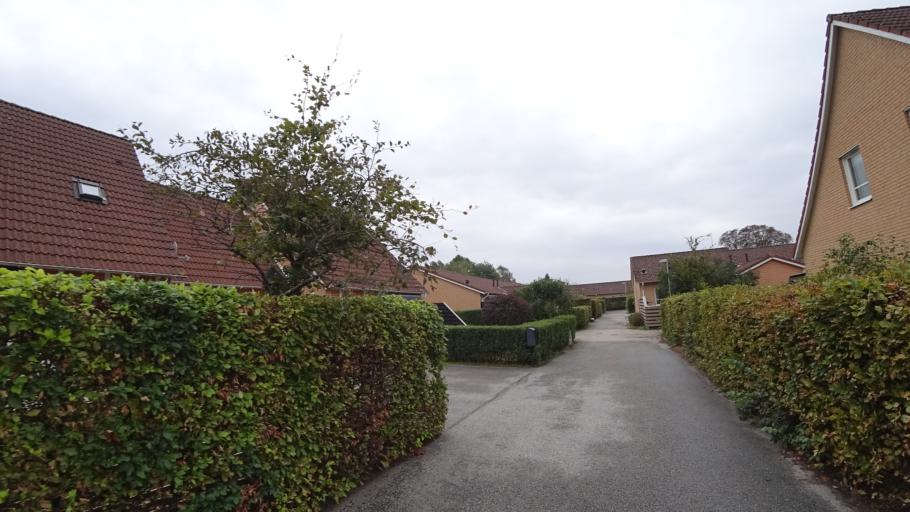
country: SE
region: Skane
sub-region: Kavlinge Kommun
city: Kaevlinge
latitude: 55.7957
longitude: 13.1378
